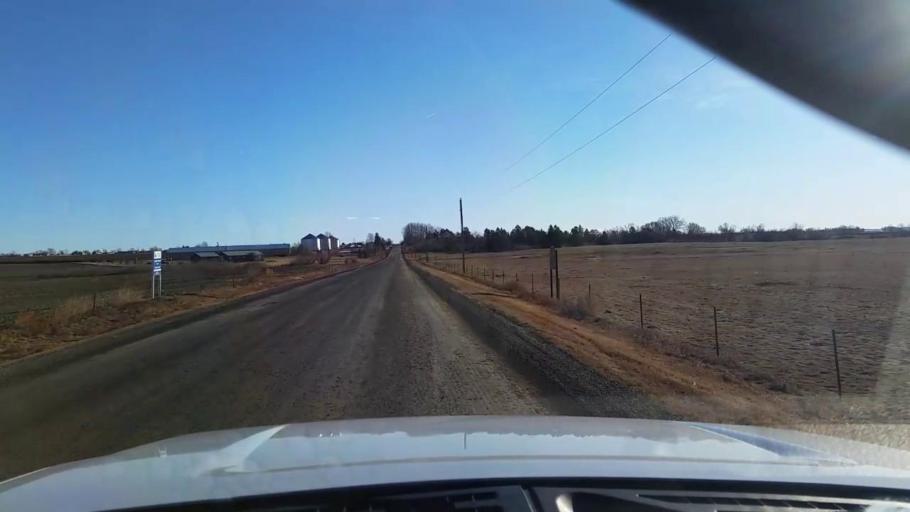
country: US
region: Colorado
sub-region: Larimer County
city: Wellington
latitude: 40.7696
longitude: -105.1005
